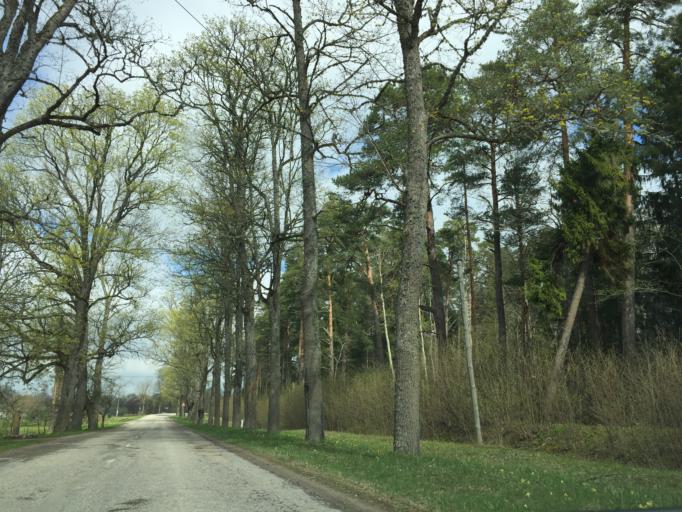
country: LV
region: Apes Novads
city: Ape
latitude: 57.5063
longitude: 26.3999
